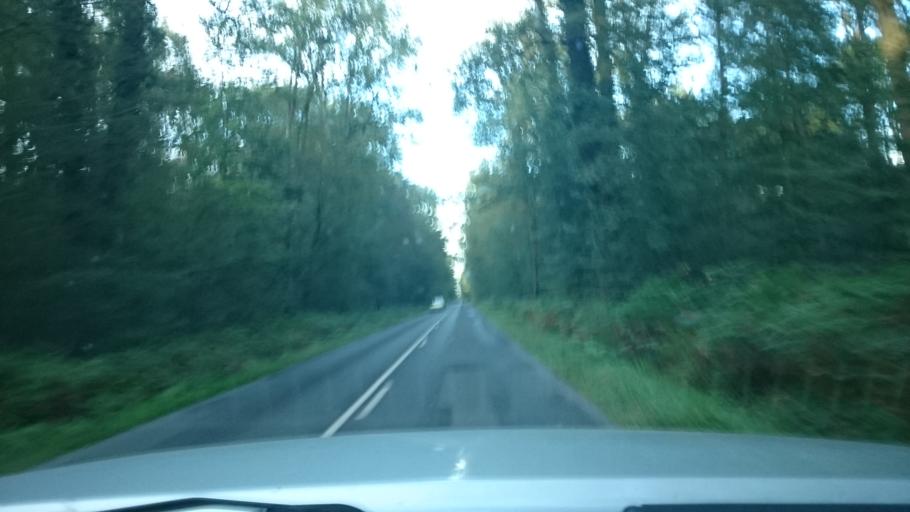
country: FR
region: Ile-de-France
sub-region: Departement de Seine-et-Marne
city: Samois-sur-Seine
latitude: 48.4587
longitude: 2.7263
